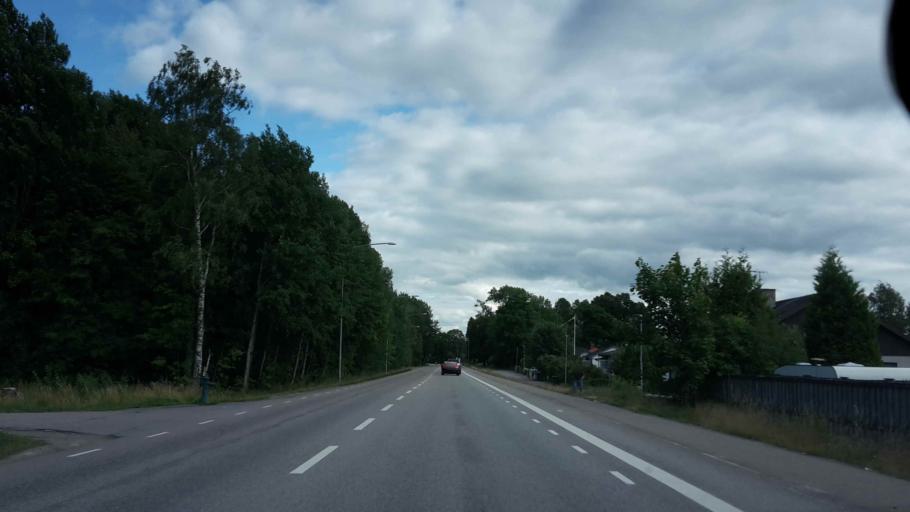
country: SE
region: OEstergoetland
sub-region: Norrkopings Kommun
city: Norrkoping
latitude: 58.6175
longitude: 16.1256
